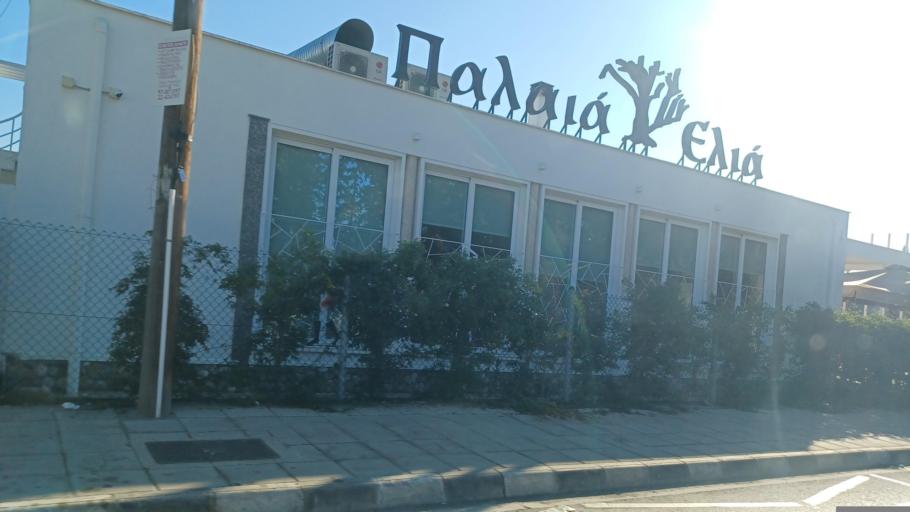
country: CY
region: Lefkosia
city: Nicosia
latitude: 35.1515
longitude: 33.3395
